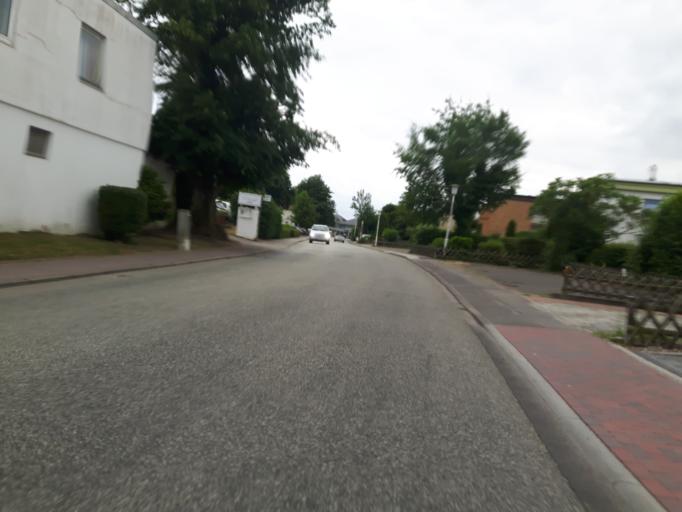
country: DE
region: Schleswig-Holstein
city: Gromitz
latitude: 54.1419
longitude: 10.9510
